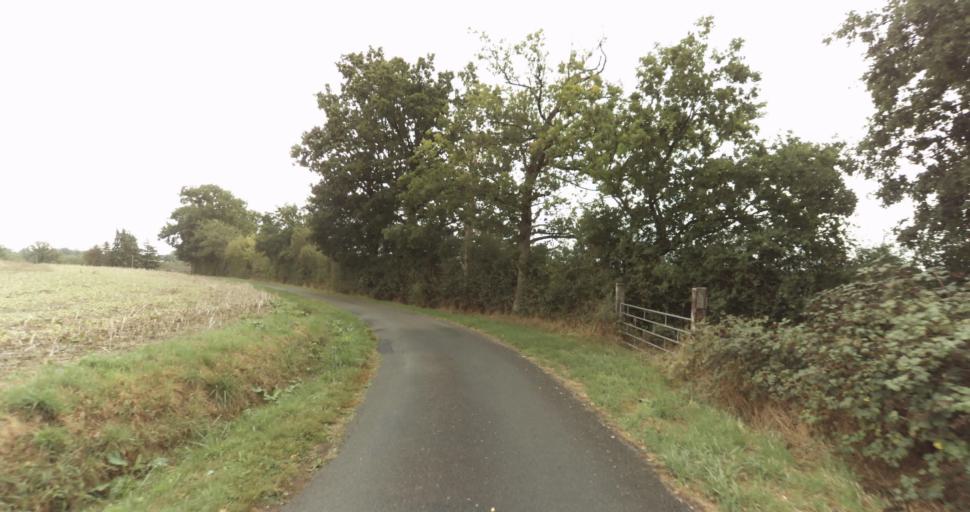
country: FR
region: Lower Normandy
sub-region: Departement de l'Orne
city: Sainte-Gauburge-Sainte-Colombe
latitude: 48.7350
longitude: 0.4767
